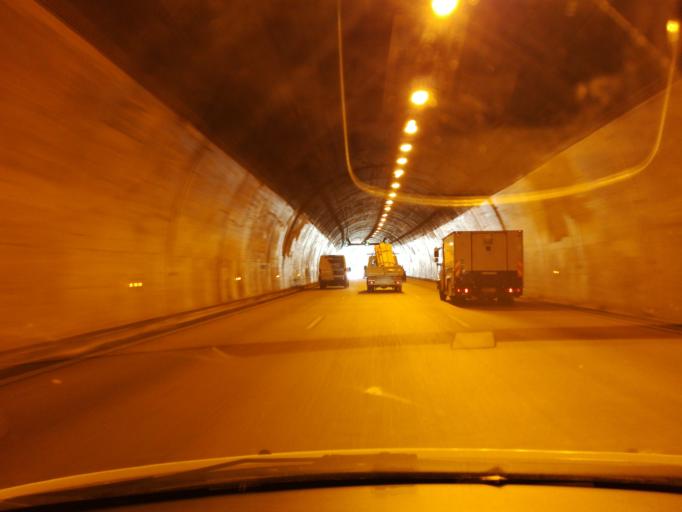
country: FR
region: Provence-Alpes-Cote d'Azur
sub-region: Departement des Alpes-Maritimes
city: Colomars
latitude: 43.7269
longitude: 7.2321
